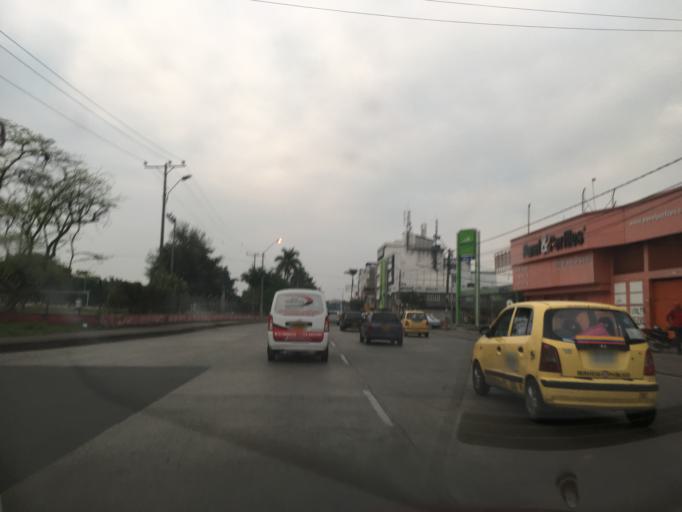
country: CO
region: Valle del Cauca
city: Cali
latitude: 3.4525
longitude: -76.5190
